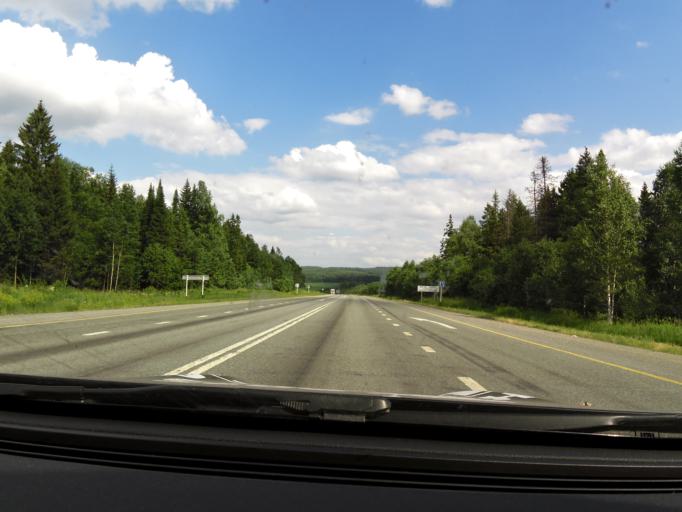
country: RU
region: Sverdlovsk
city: Bisert'
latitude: 56.8269
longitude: 59.1517
